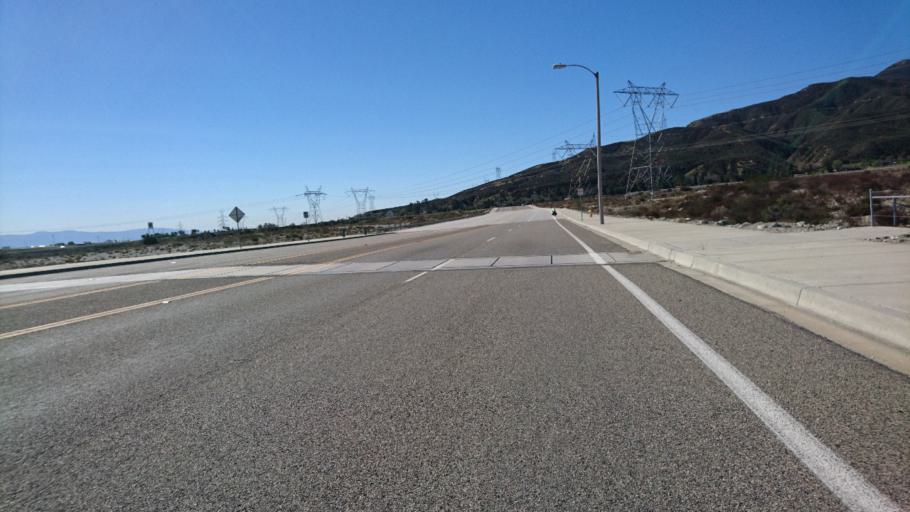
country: US
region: California
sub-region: San Bernardino County
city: Muscoy
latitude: 34.1902
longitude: -117.4328
